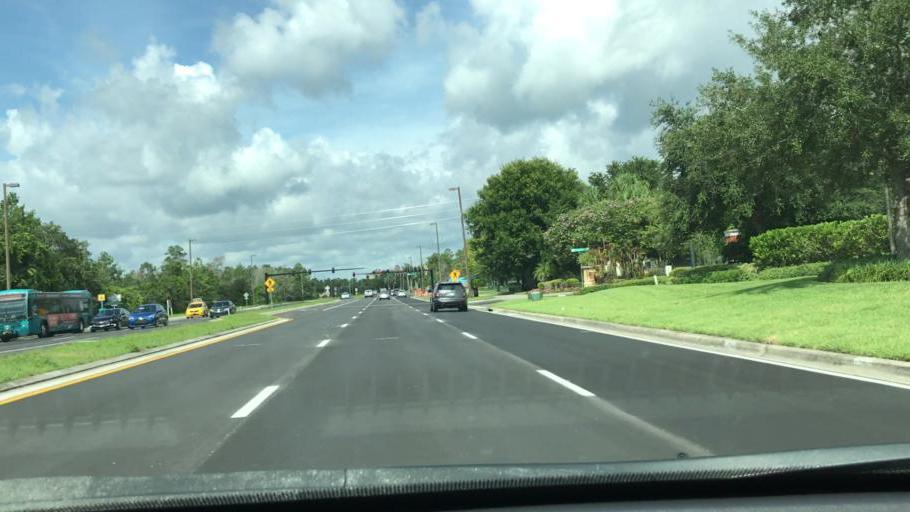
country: US
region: Florida
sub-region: Orange County
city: Williamsburg
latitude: 28.3865
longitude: -81.4809
